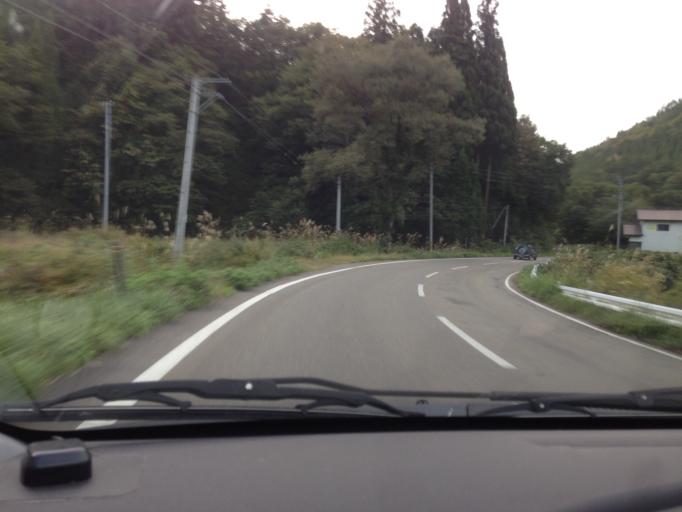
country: JP
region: Fukushima
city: Kitakata
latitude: 37.3749
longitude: 139.5527
